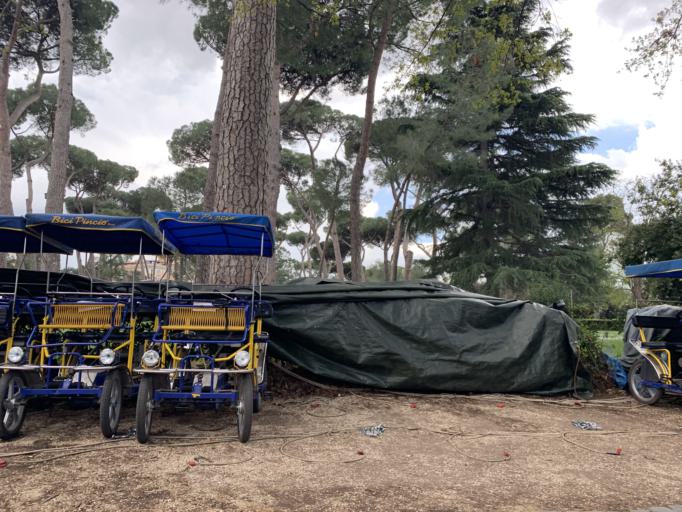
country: IT
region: Latium
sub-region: Citta metropolitana di Roma Capitale
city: Rome
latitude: 41.9111
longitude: 12.4886
